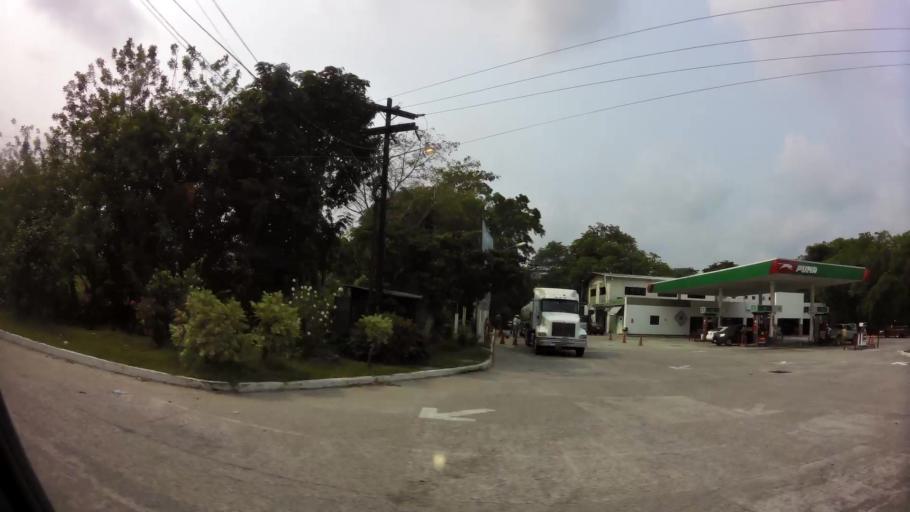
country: HN
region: Atlantida
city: Tela
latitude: 15.7600
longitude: -87.4864
